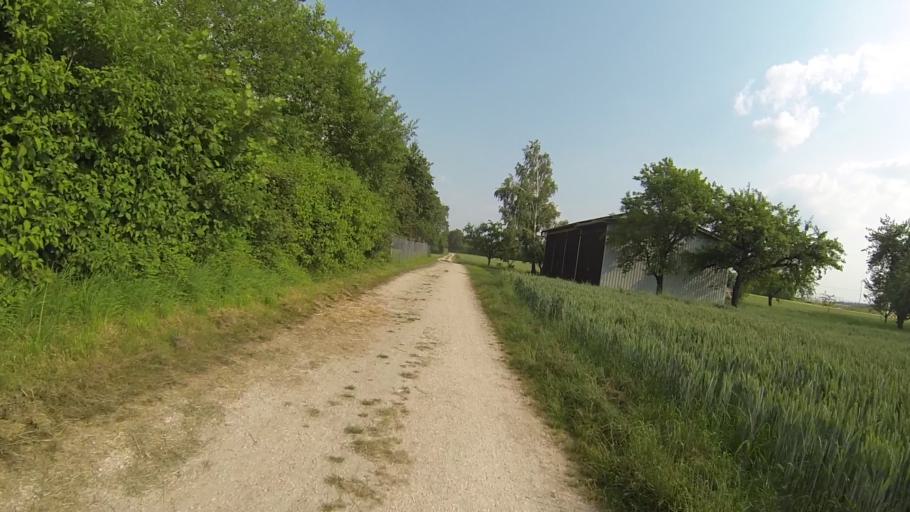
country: DE
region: Baden-Wuerttemberg
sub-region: Tuebingen Region
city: Beimerstetten
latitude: 48.4460
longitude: 9.9827
